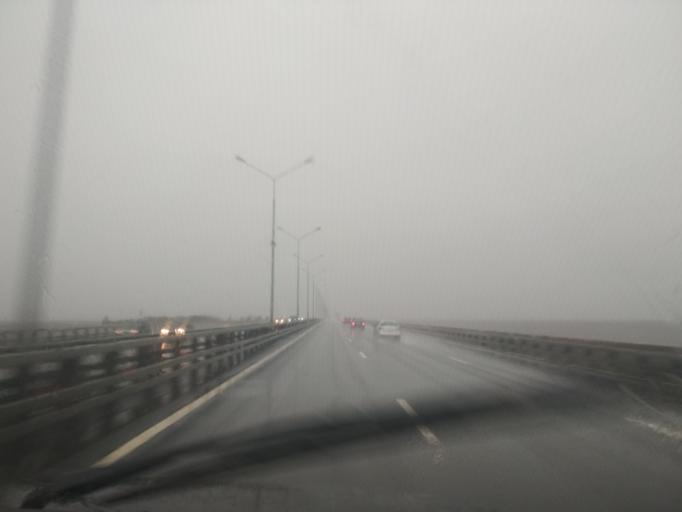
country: RU
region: Leningrad
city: Gorskaya
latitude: 60.0353
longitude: 29.9345
